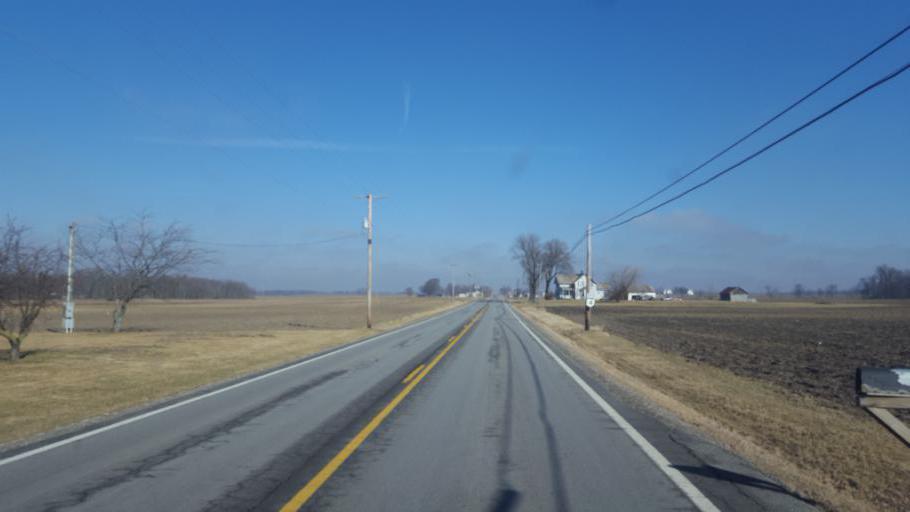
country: US
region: Ohio
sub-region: Crawford County
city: Bucyrus
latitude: 40.8632
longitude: -82.9648
